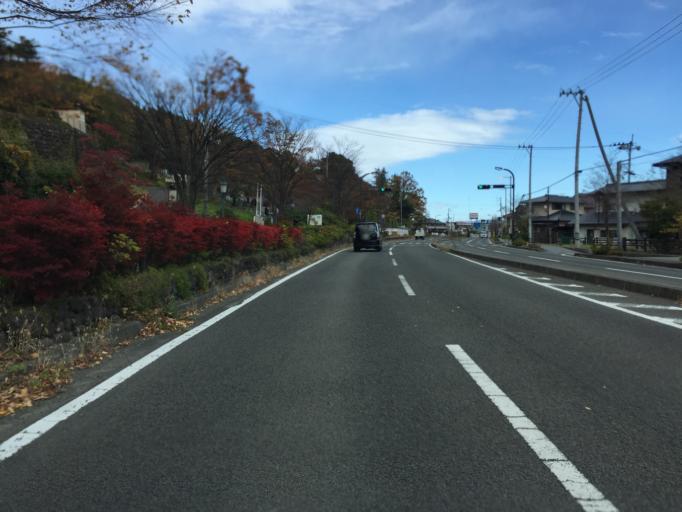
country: JP
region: Fukushima
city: Fukushima-shi
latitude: 37.7706
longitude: 140.4790
